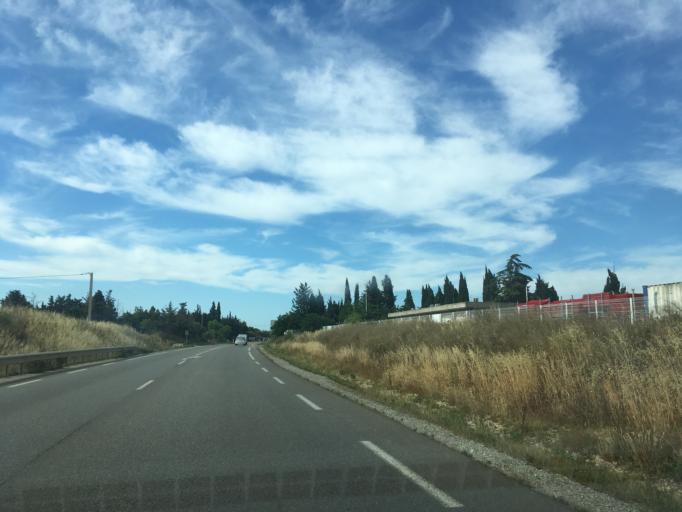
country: FR
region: Languedoc-Roussillon
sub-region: Departement du Gard
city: Bouillargues
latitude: 43.7882
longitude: 4.4292
